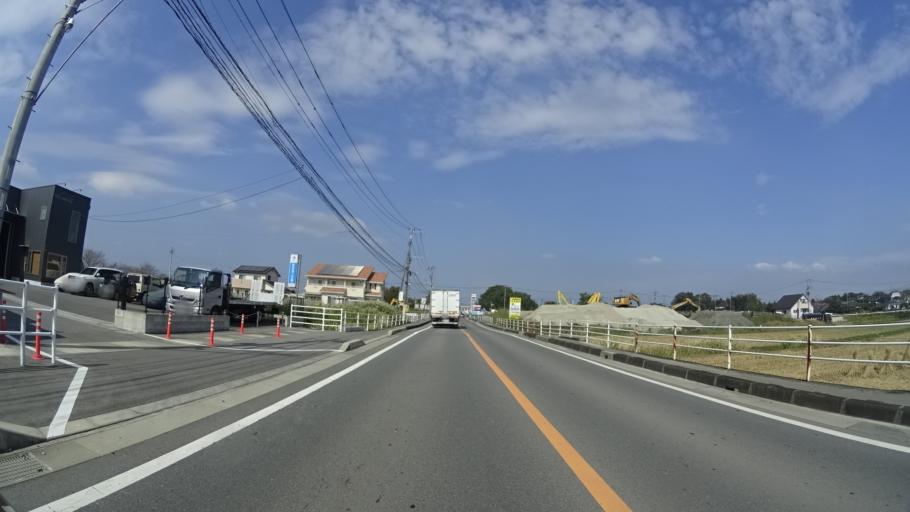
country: JP
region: Kumamoto
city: Kumamoto
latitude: 32.7440
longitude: 130.7713
